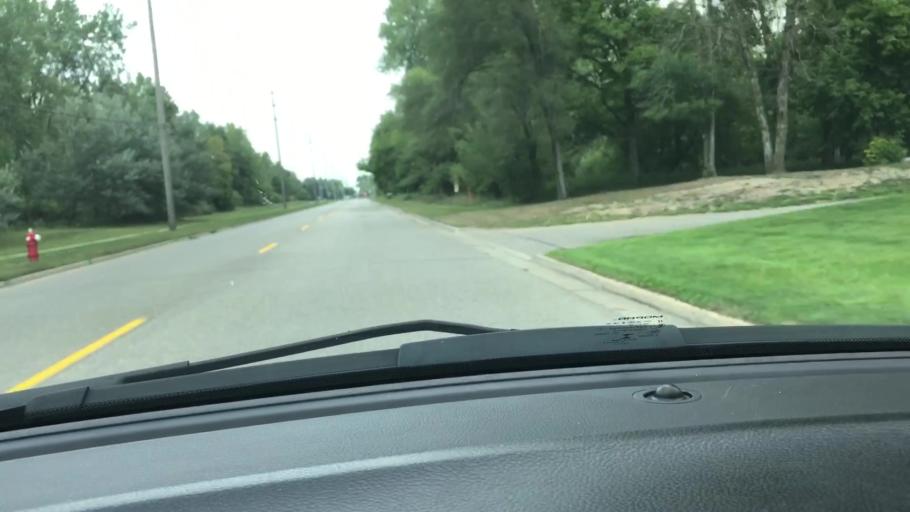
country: US
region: Michigan
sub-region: Midland County
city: Midland
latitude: 43.6178
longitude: -84.1874
